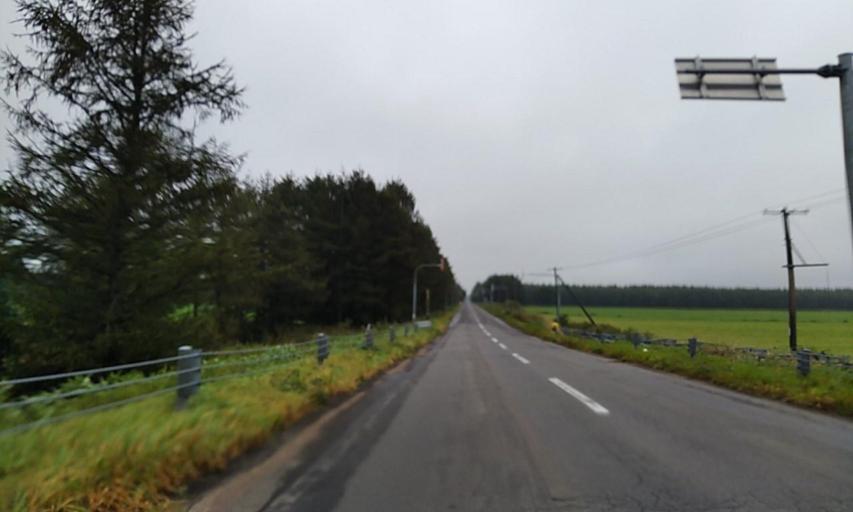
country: JP
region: Hokkaido
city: Shibetsu
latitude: 43.5051
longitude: 144.6620
